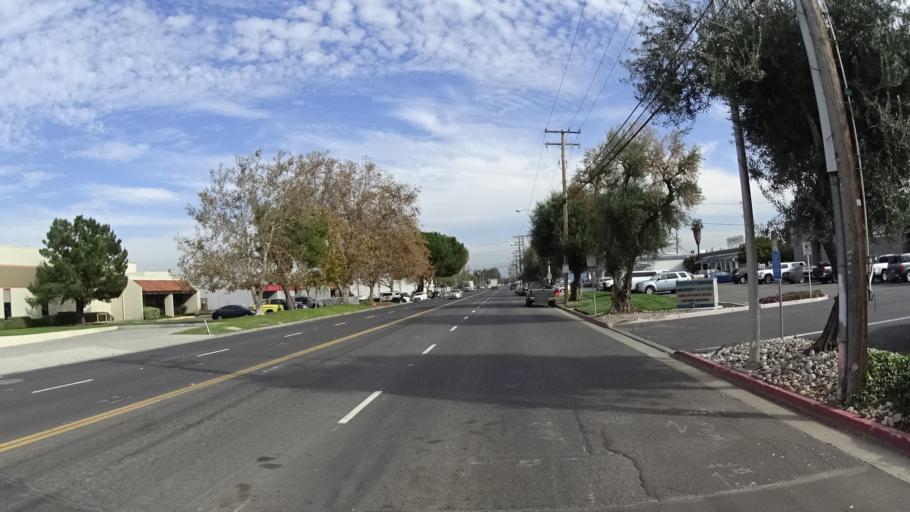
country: US
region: California
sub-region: Santa Clara County
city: Santa Clara
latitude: 37.3662
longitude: -121.9566
